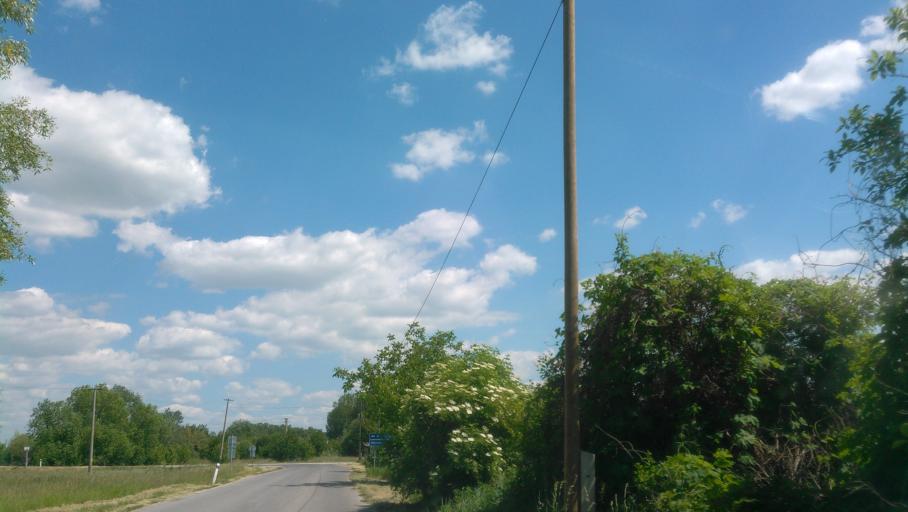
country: SK
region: Nitriansky
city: Kolarovo
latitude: 47.8747
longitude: 17.9165
